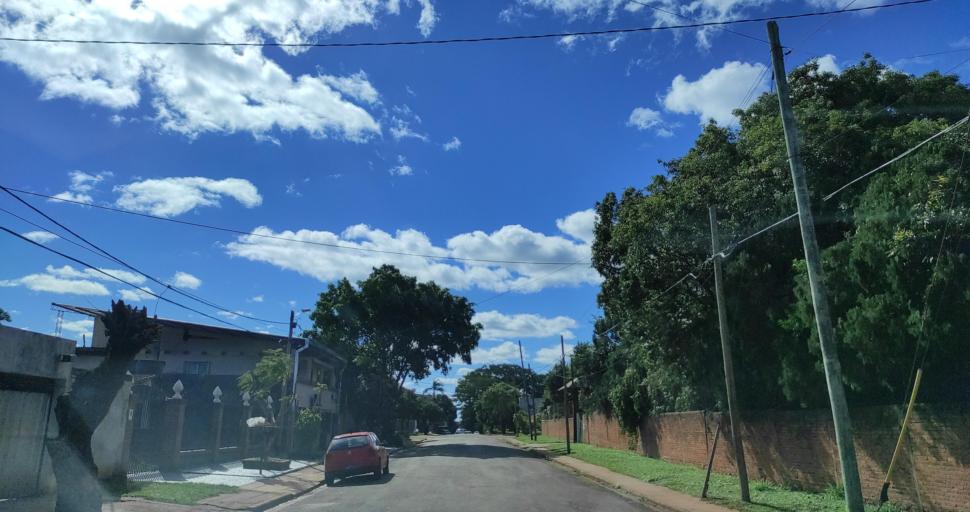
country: AR
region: Misiones
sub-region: Departamento de Capital
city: Posadas
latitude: -27.3687
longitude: -55.9339
